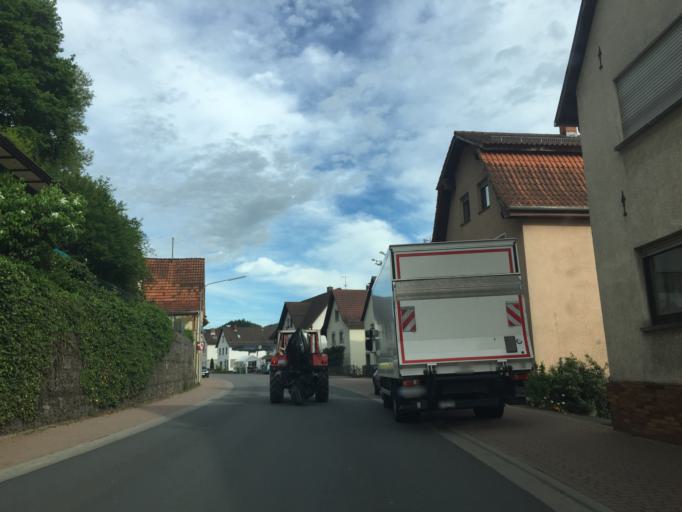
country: DE
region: Hesse
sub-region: Regierungsbezirk Darmstadt
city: Birkenau
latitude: 49.5340
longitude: 8.7228
